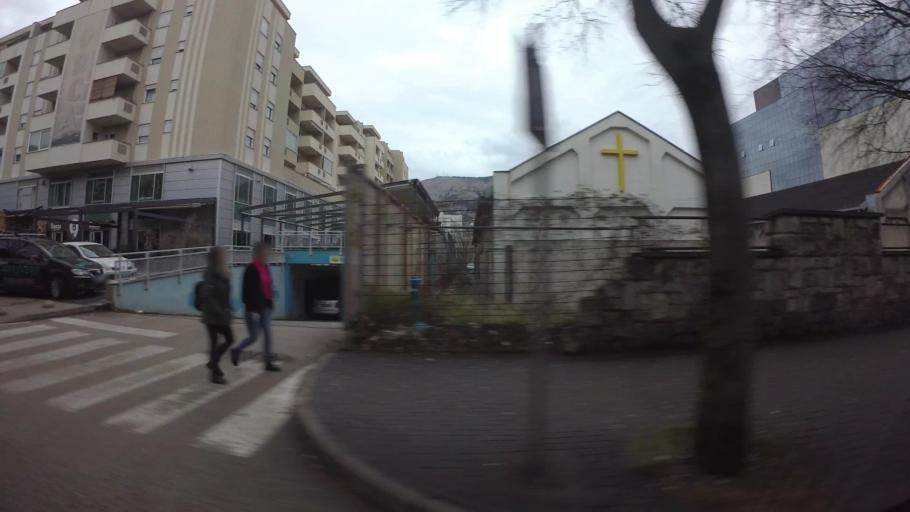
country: BA
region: Federation of Bosnia and Herzegovina
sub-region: Hercegovacko-Bosanski Kanton
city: Mostar
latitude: 43.3495
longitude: 17.8042
